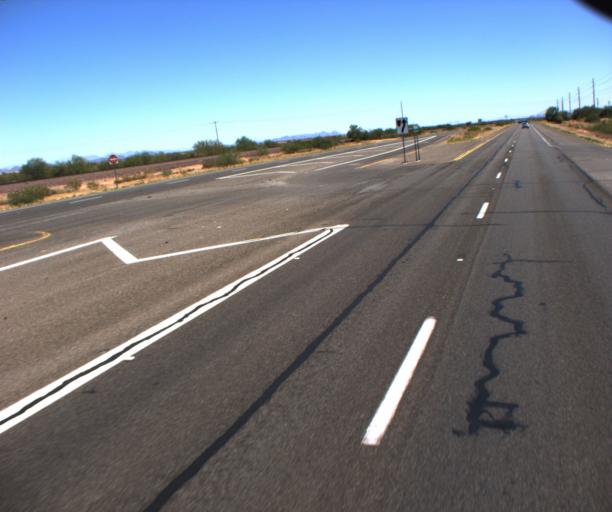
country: US
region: Arizona
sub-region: Maricopa County
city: Sun City West
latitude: 33.7138
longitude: -112.4467
